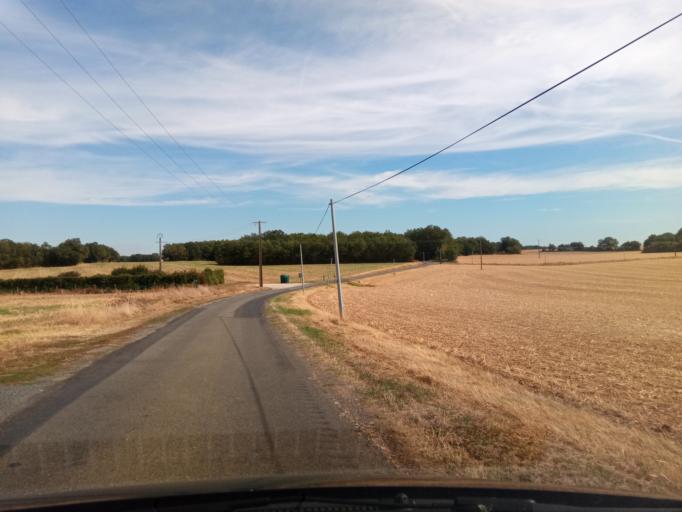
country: FR
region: Poitou-Charentes
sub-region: Departement de la Vienne
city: Chauvigny
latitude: 46.5531
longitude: 0.7475
